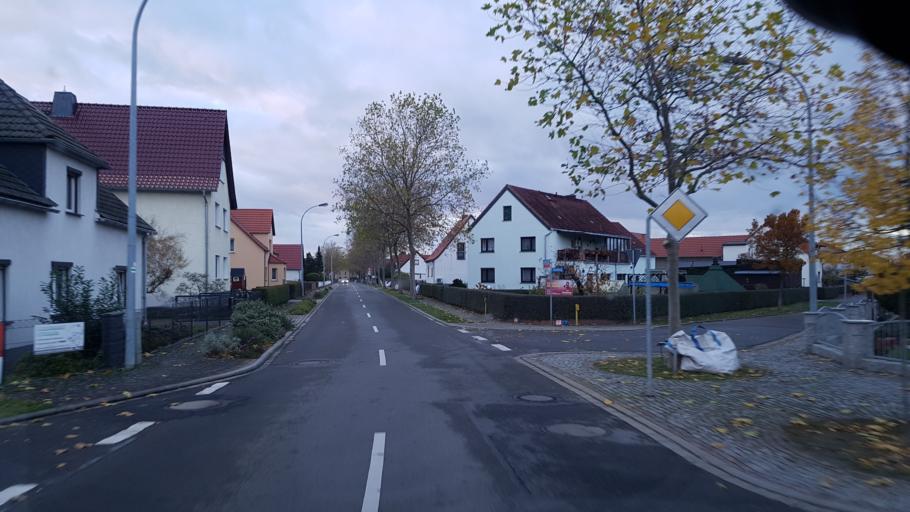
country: DE
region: Brandenburg
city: Tettau
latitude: 51.4290
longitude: 13.7346
